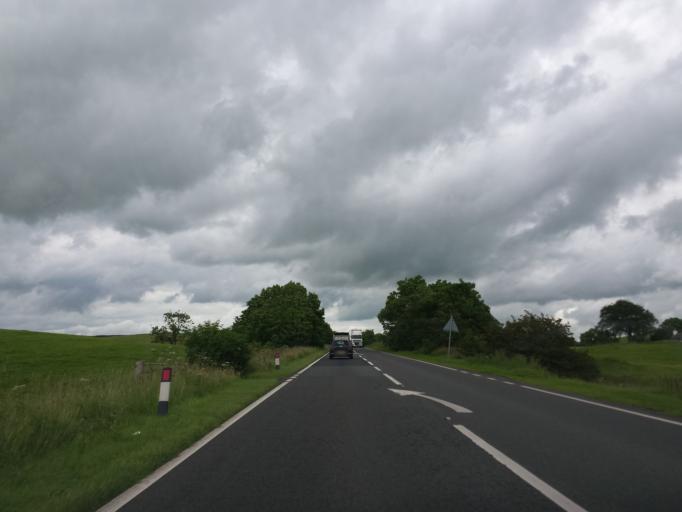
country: GB
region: Scotland
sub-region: Dumfries and Galloway
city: Castle Douglas
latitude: 55.0005
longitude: -3.8793
